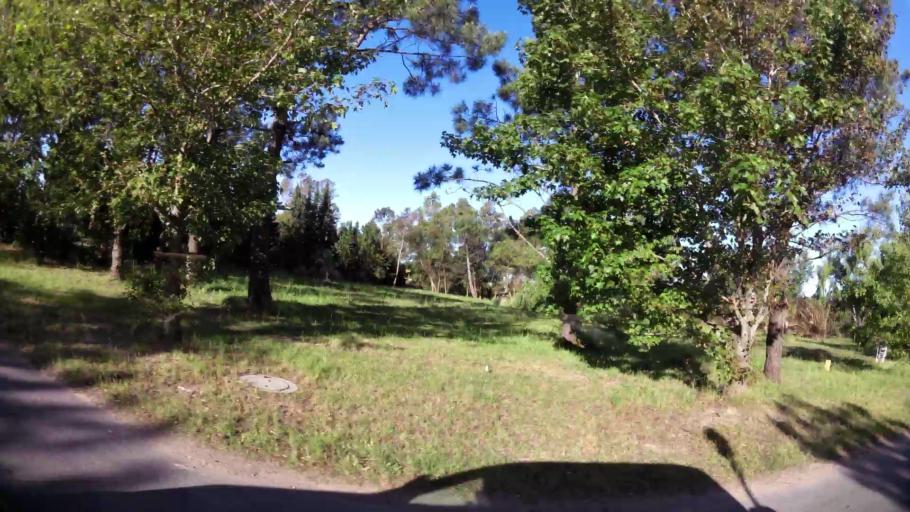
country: UY
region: Canelones
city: Barra de Carrasco
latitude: -34.8712
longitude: -56.0420
